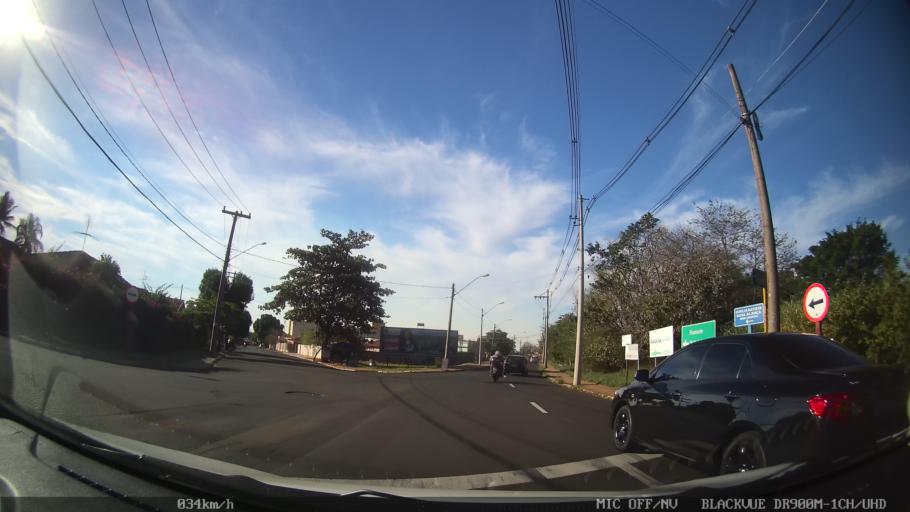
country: BR
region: Sao Paulo
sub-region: Araraquara
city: Araraquara
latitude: -21.7677
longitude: -48.1631
